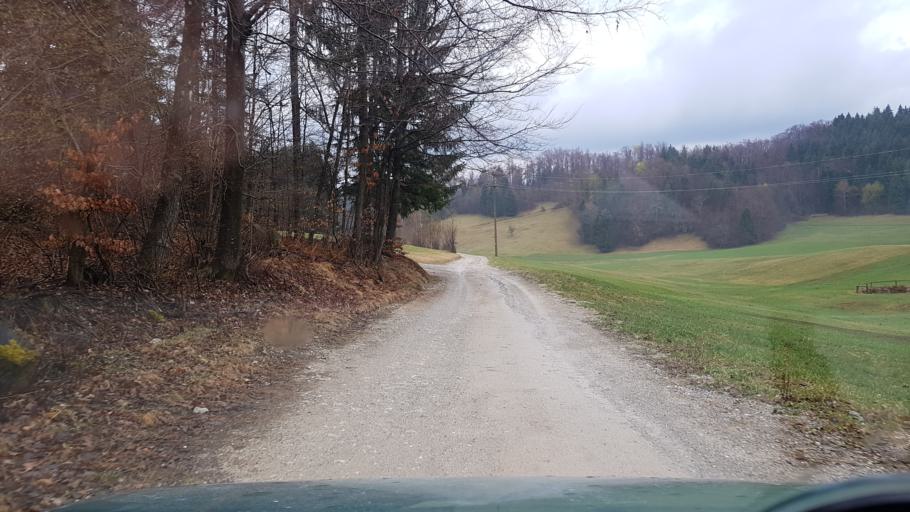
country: SI
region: Tolmin
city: Tolmin
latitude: 46.1373
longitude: 13.8470
